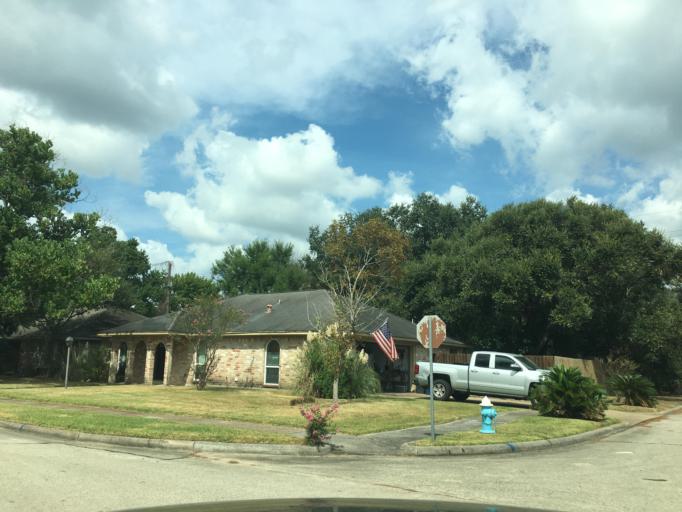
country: US
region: Texas
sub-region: Harris County
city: Spring
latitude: 30.1184
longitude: -95.3982
